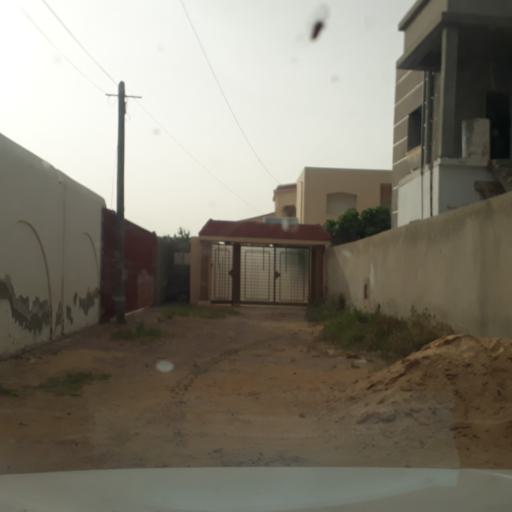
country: TN
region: Safaqis
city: Al Qarmadah
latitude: 34.8162
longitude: 10.7726
